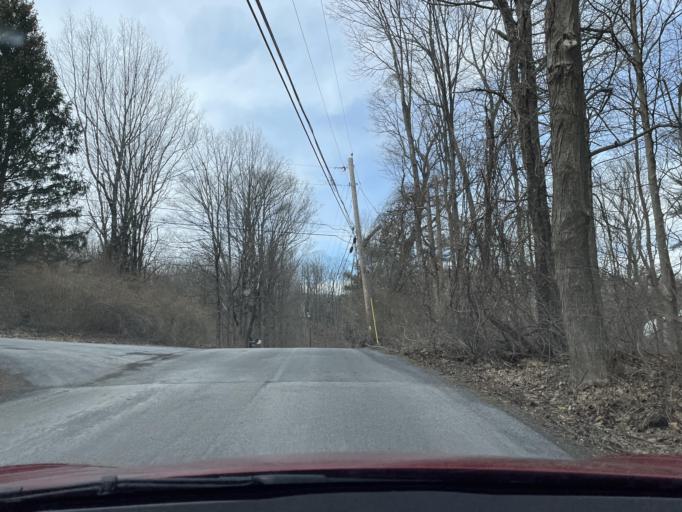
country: US
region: New York
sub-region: Ulster County
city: Manorville
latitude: 42.1082
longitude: -73.9960
